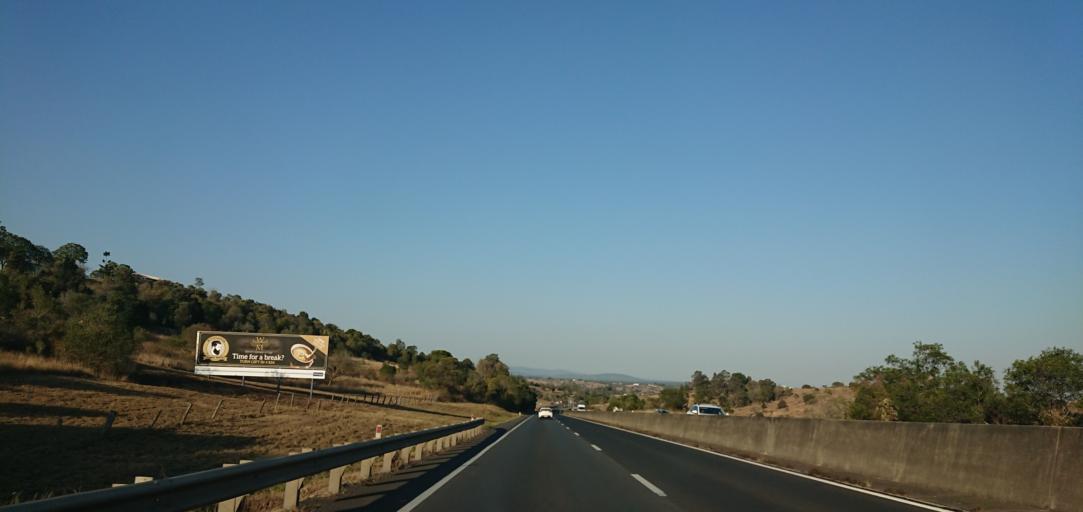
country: AU
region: Queensland
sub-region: Ipswich
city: Thagoona
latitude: -27.5652
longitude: 152.5693
